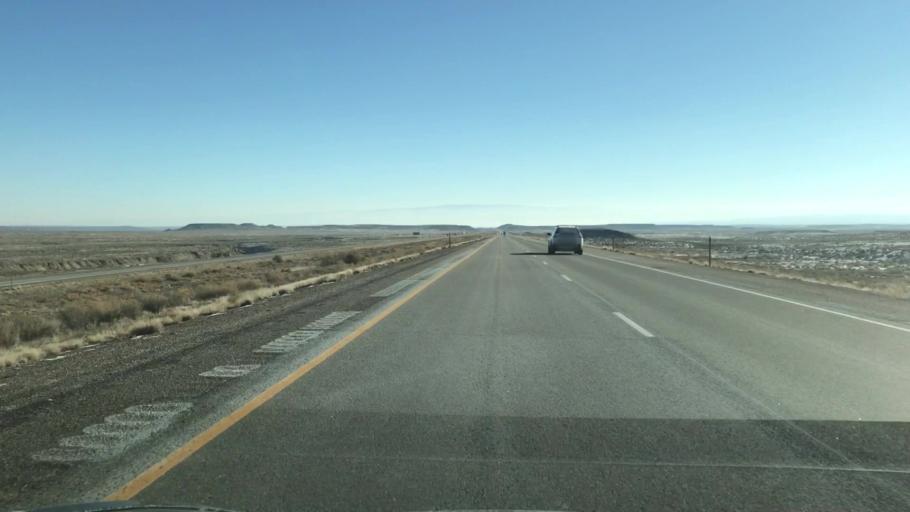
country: US
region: Utah
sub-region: Grand County
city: Moab
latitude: 38.9484
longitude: -109.6699
